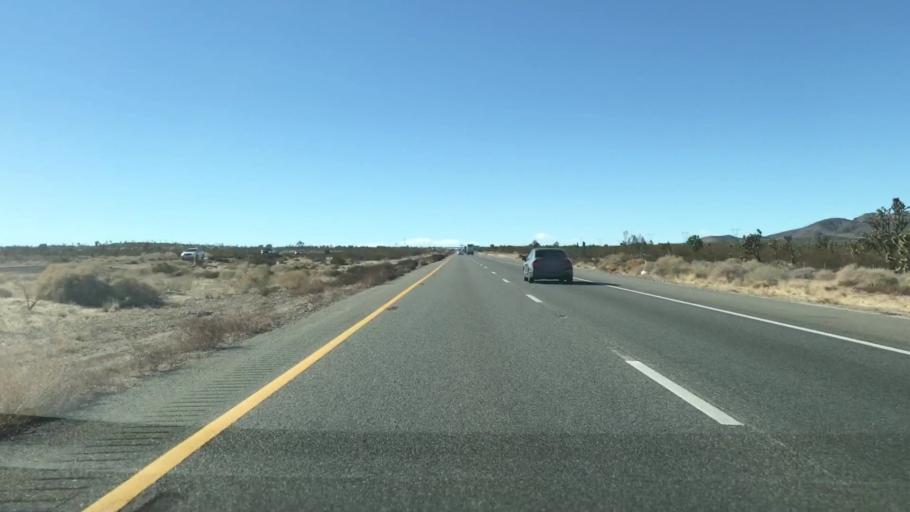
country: US
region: Nevada
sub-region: Clark County
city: Sandy Valley
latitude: 35.4128
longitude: -115.7633
